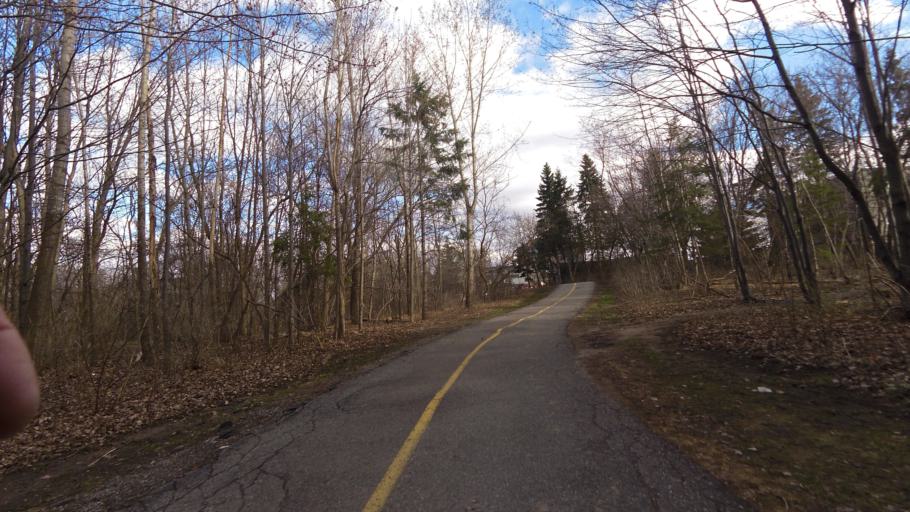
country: CA
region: Ontario
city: Bells Corners
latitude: 45.3521
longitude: -75.7667
